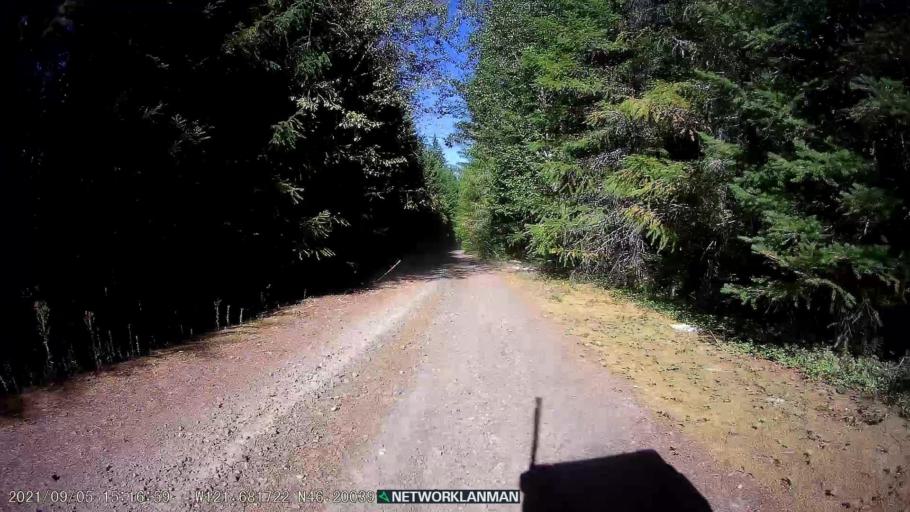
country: US
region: Washington
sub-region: Skamania County
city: Carson
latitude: 46.2003
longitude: -121.6818
